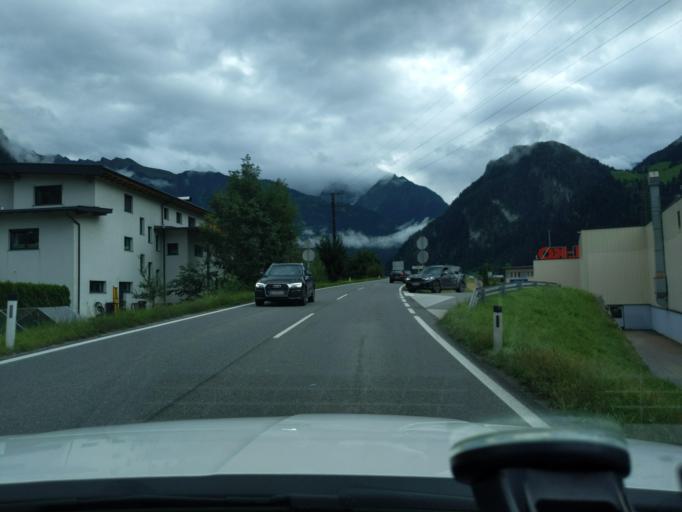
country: AT
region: Tyrol
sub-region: Politischer Bezirk Schwaz
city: Ramsau im Zillertal
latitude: 47.1924
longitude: 11.8706
